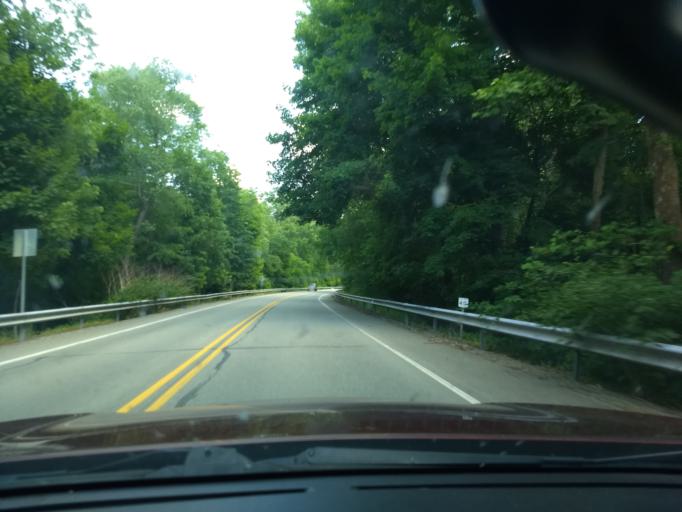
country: US
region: Pennsylvania
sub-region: Westmoreland County
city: Trafford
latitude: 40.3714
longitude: -79.7534
